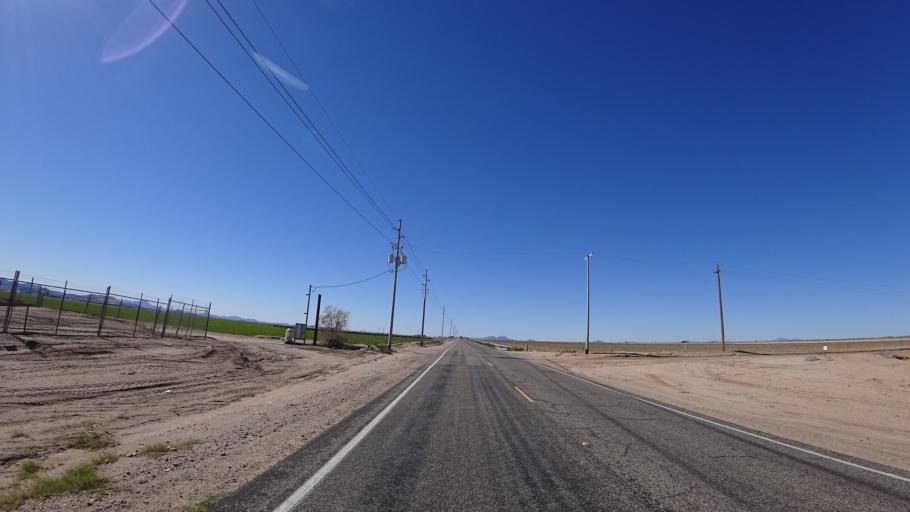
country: US
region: Arizona
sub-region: Maricopa County
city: Buckeye
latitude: 33.3921
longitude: -112.6166
